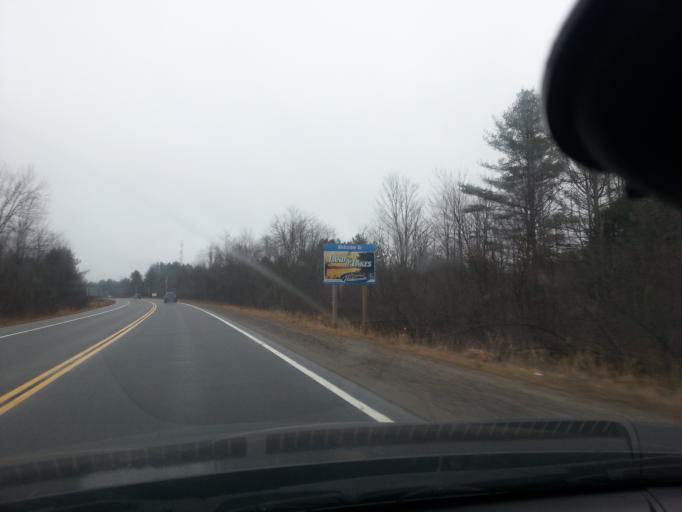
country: CA
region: Ontario
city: Belleville
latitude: 44.5415
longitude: -77.3523
